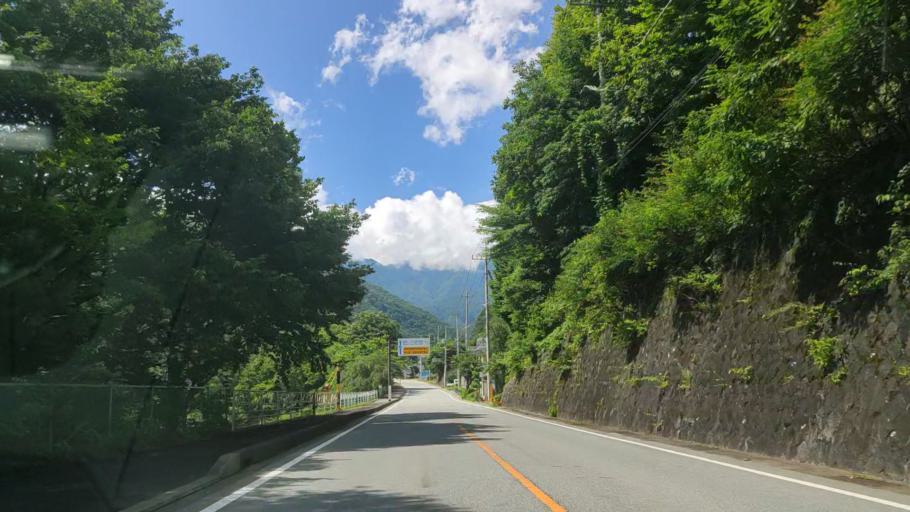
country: JP
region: Yamanashi
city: Enzan
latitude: 35.8463
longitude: 138.7623
